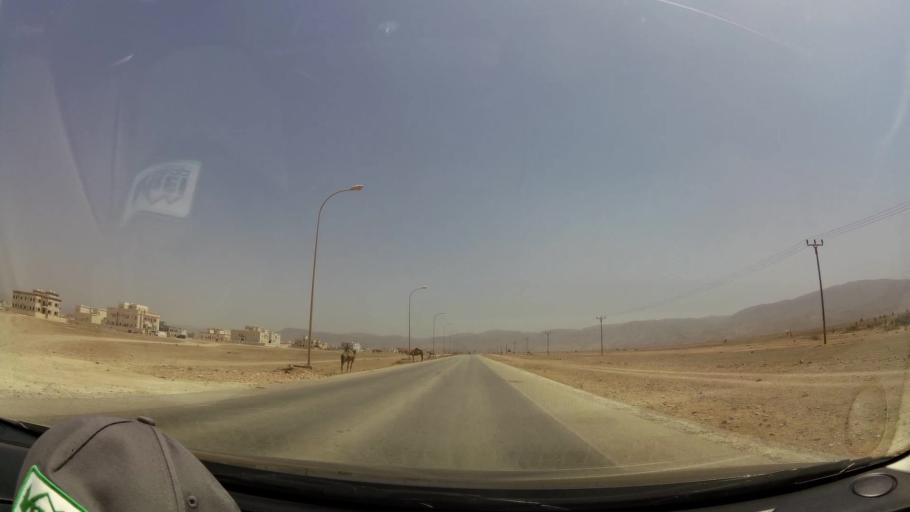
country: OM
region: Zufar
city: Salalah
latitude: 17.0831
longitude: 54.2170
